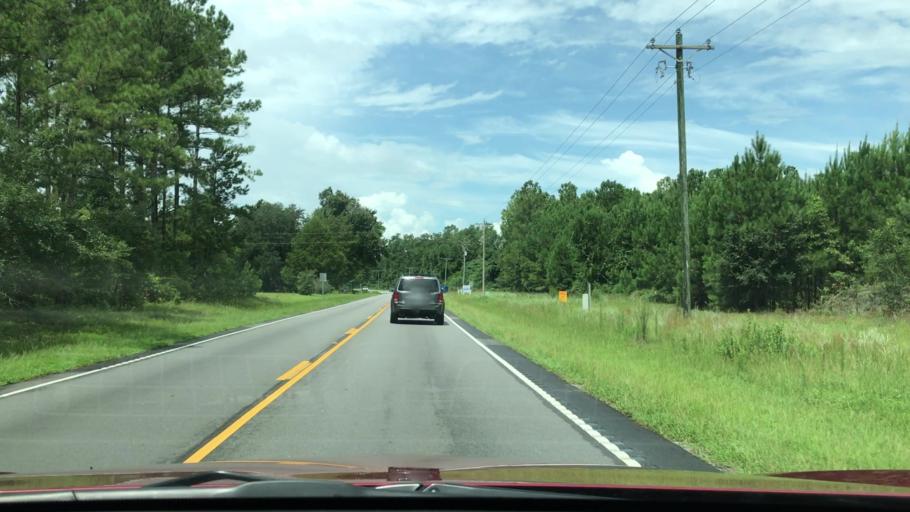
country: US
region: South Carolina
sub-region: Horry County
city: Red Hill
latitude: 33.9036
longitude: -78.9066
